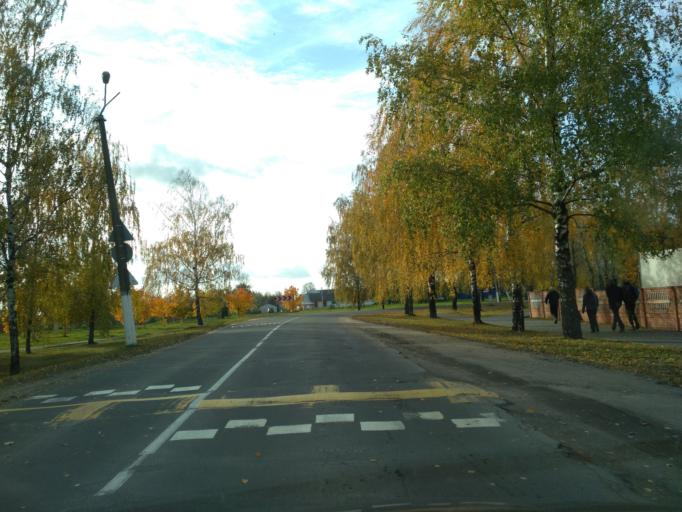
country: BY
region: Minsk
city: Mar''ina Horka
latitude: 53.5048
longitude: 28.1575
